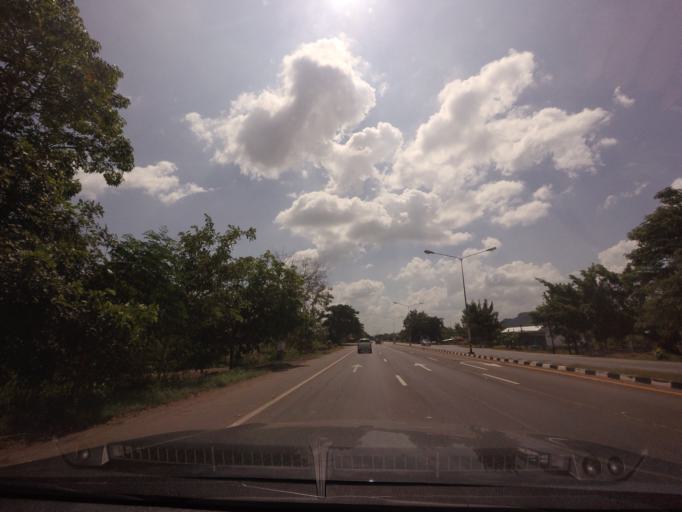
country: TH
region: Phetchabun
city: Nong Phai
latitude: 16.1343
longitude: 101.0475
